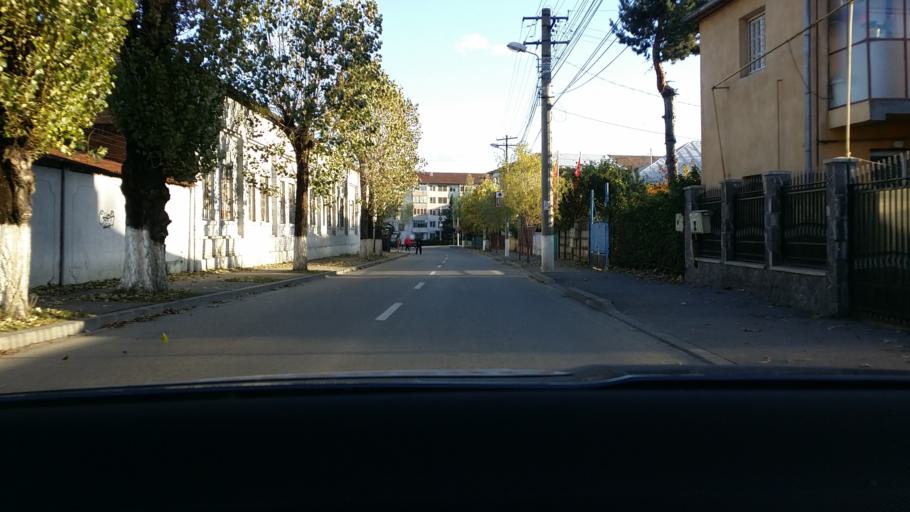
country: RO
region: Prahova
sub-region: Municipiul Campina
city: Campina
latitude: 45.1294
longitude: 25.7359
